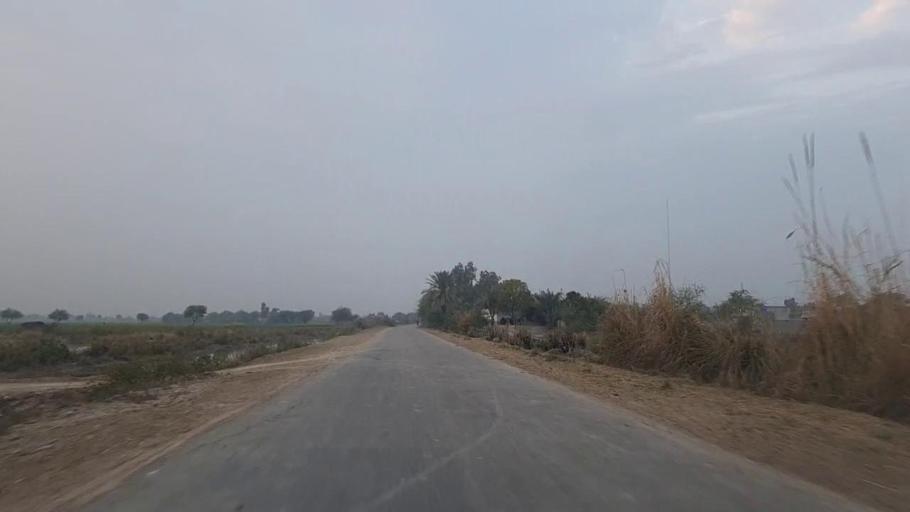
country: PK
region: Sindh
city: Jam Sahib
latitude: 26.3206
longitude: 68.5546
